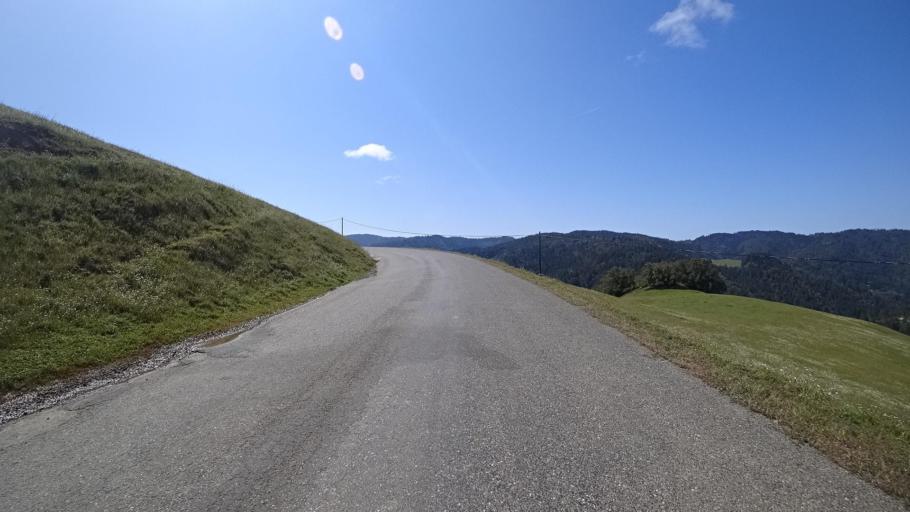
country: US
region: California
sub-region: Humboldt County
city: Redway
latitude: 40.0266
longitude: -123.6326
